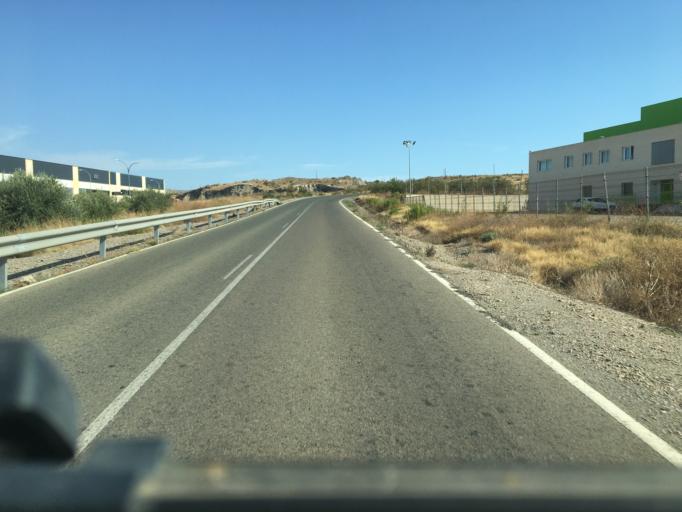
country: ES
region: Andalusia
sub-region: Provincia de Almeria
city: Huercal-Overa
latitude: 37.4198
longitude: -1.9689
